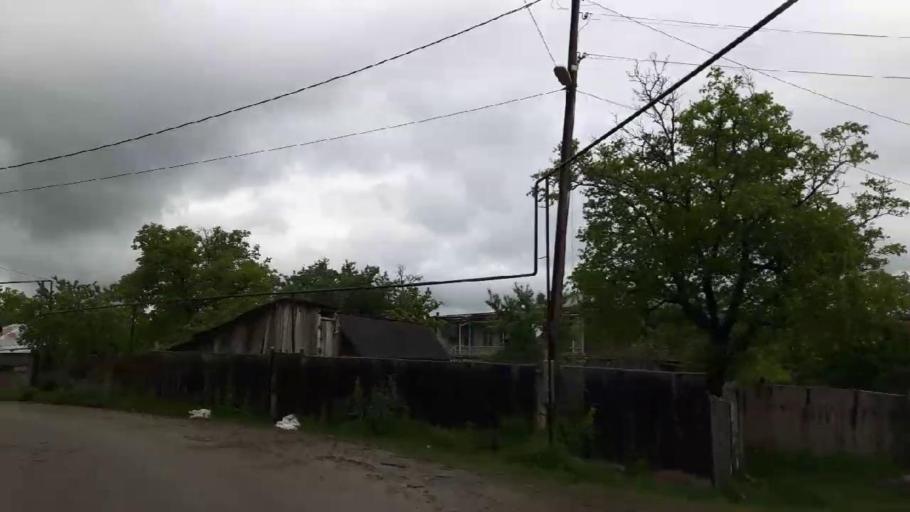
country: GE
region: Shida Kartli
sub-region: Khashuris Raioni
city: Khashuri
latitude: 41.9825
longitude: 43.6691
